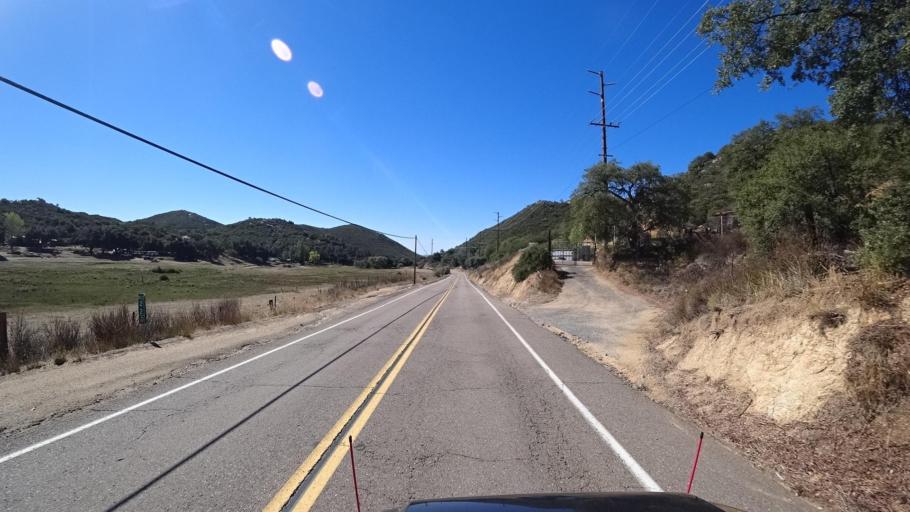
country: US
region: California
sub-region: San Diego County
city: Descanso
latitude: 32.8204
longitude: -116.6292
